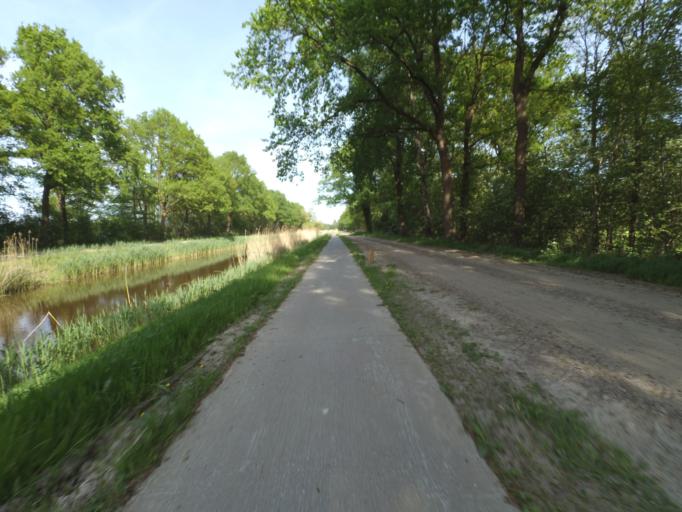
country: NL
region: Overijssel
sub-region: Gemeente Tubbergen
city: Tubbergen
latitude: 52.3654
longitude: 6.7918
